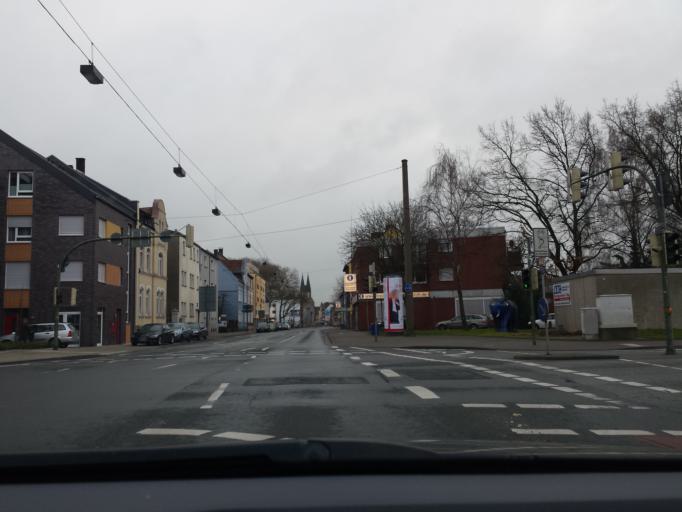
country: DE
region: North Rhine-Westphalia
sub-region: Regierungsbezirk Arnsberg
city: Hamm
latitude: 51.6722
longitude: 7.8170
